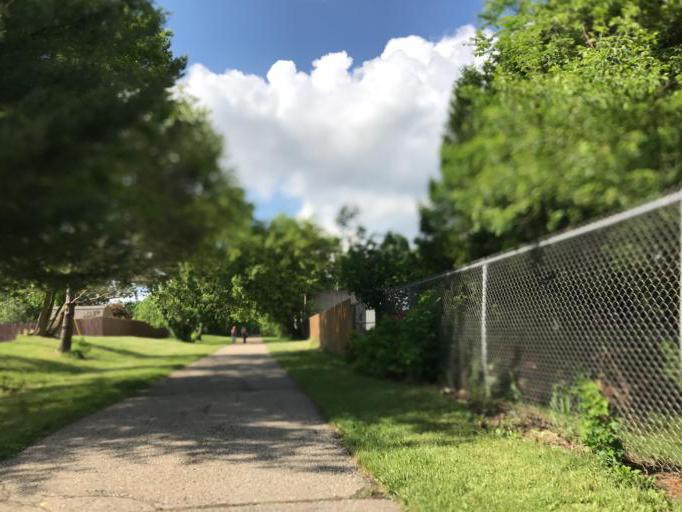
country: US
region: Michigan
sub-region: Oakland County
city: South Lyon
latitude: 42.4617
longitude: -83.6465
